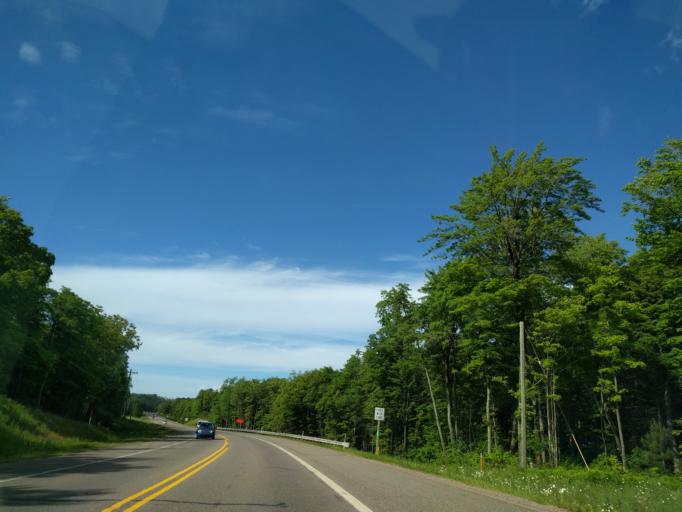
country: US
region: Michigan
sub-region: Marquette County
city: Harvey
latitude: 46.4791
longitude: -87.4178
